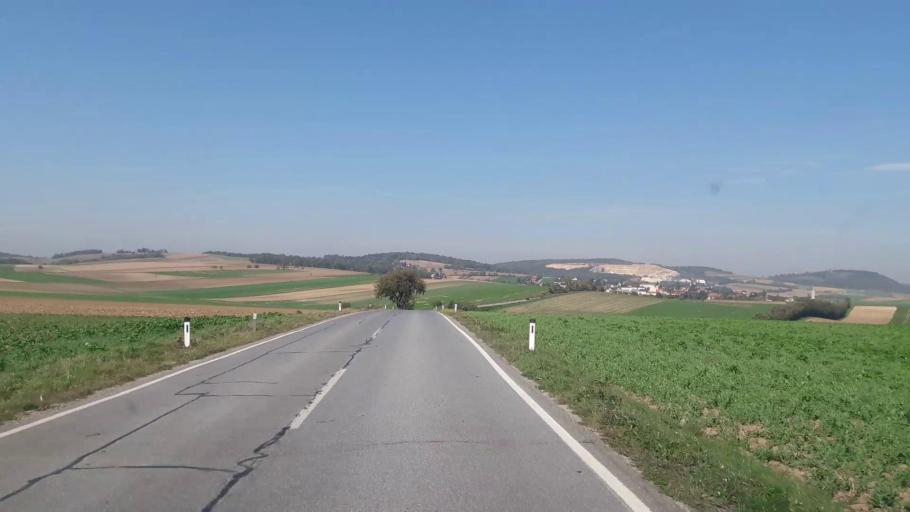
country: AT
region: Lower Austria
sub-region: Politischer Bezirk Korneuburg
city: Ernstbrunn
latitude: 48.5082
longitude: 16.3621
